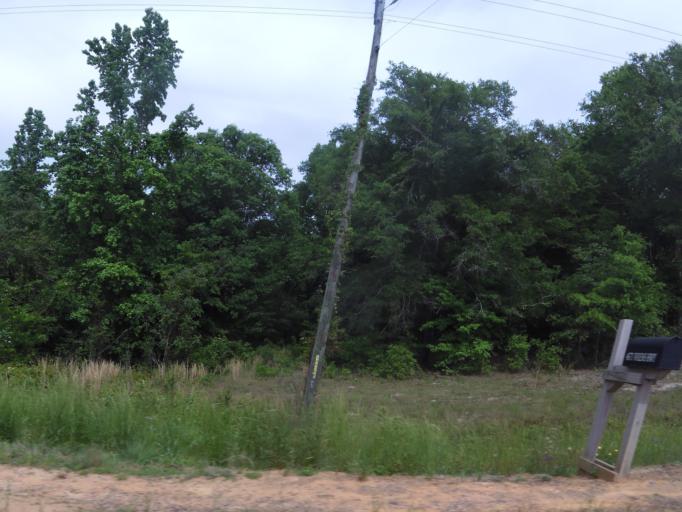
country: US
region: Georgia
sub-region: McDuffie County
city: Thomson
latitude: 33.3517
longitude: -82.4616
